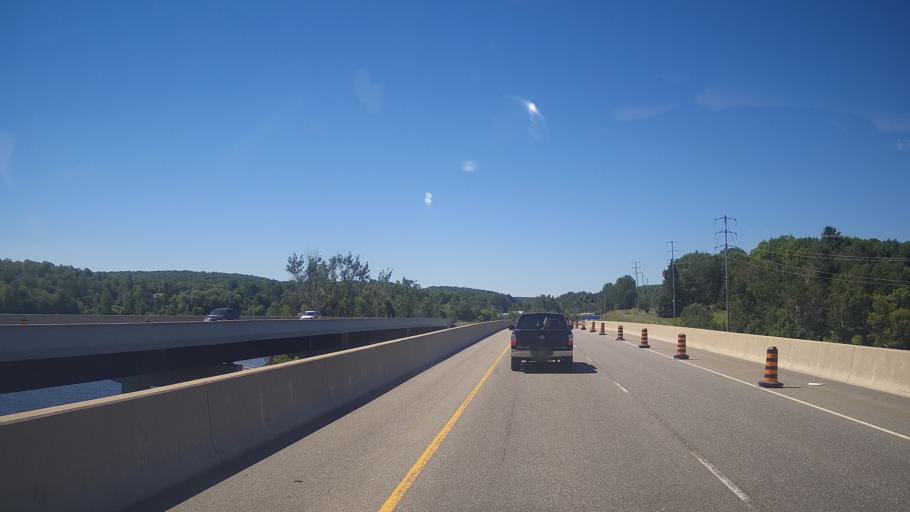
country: CA
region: Ontario
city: Huntsville
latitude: 45.3250
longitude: -79.2397
